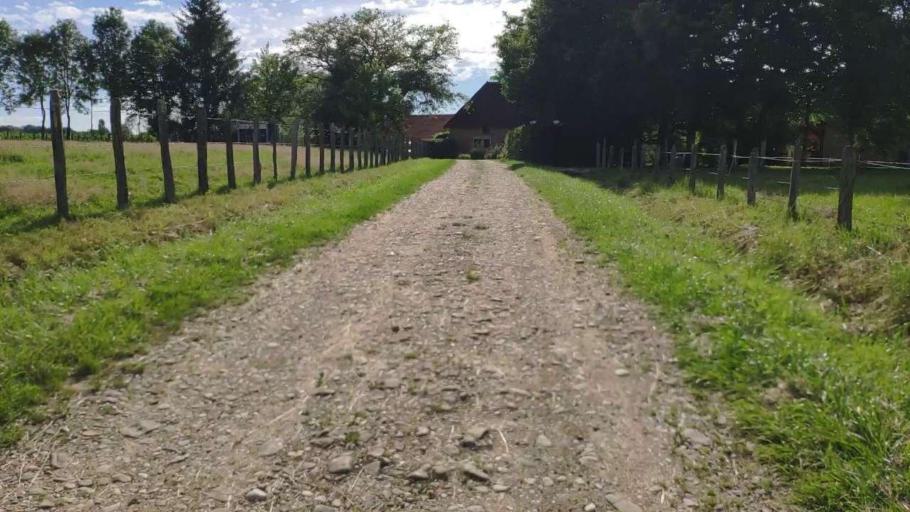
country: FR
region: Franche-Comte
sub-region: Departement du Jura
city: Bletterans
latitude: 46.8105
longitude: 5.5064
